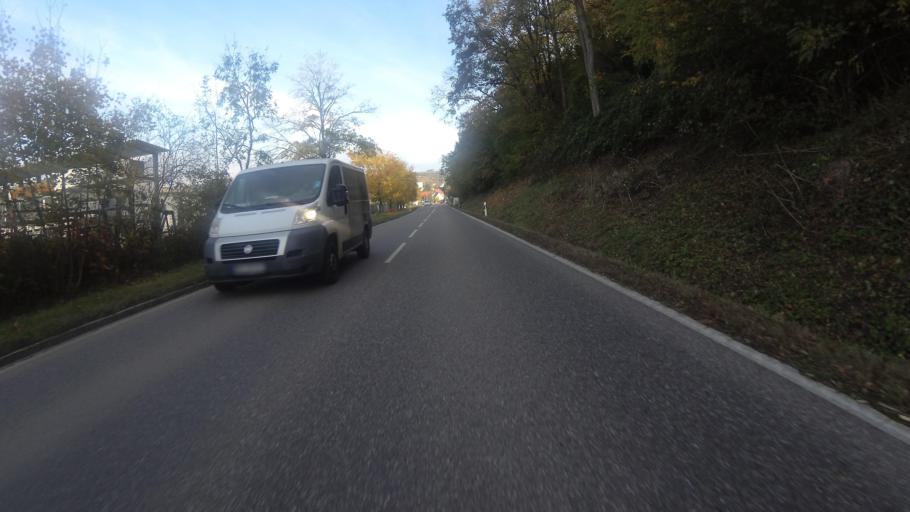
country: DE
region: Baden-Wuerttemberg
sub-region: Regierungsbezirk Stuttgart
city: Mockmuhl
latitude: 49.3168
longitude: 9.3637
